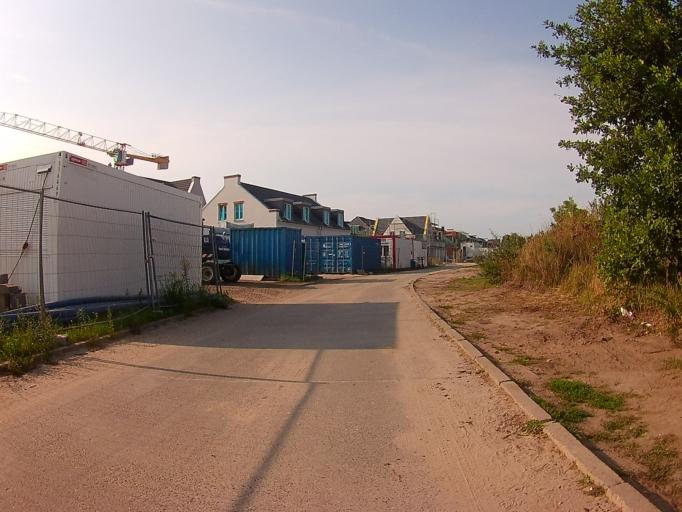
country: DE
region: Berlin
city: Kaulsdorf
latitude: 52.5021
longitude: 13.5772
